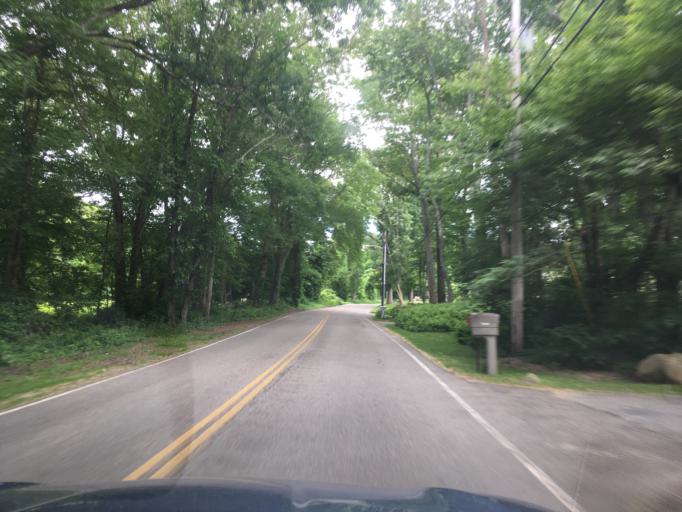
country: US
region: Rhode Island
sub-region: Washington County
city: Exeter
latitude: 41.6143
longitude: -71.5095
